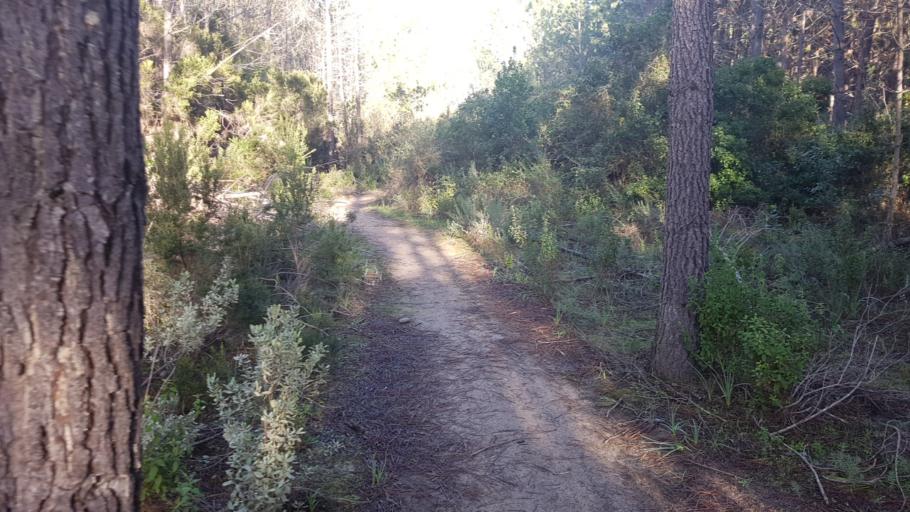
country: FR
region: Corsica
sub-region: Departement de la Haute-Corse
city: Ghisonaccia
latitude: 42.0168
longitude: 9.4681
